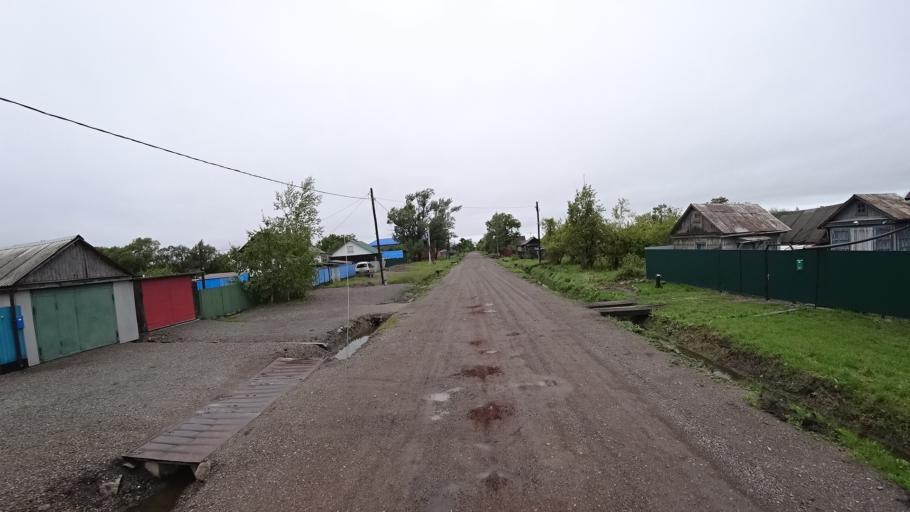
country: RU
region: Primorskiy
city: Monastyrishche
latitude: 44.2093
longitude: 132.4343
